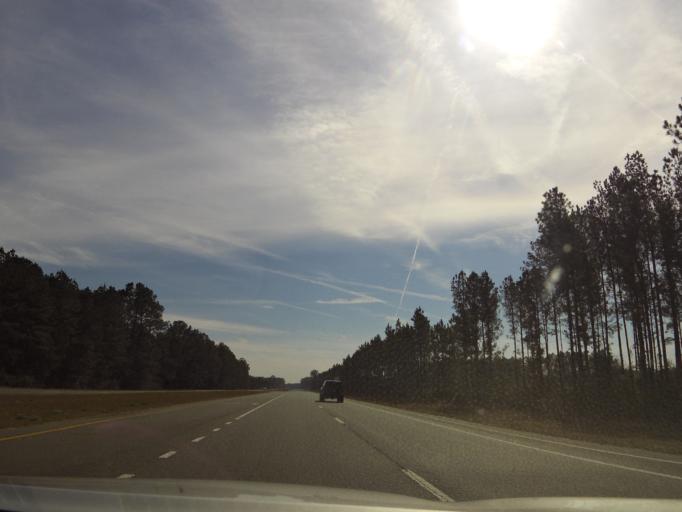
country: US
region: Georgia
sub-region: Ware County
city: Waycross
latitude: 31.1433
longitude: -82.2773
